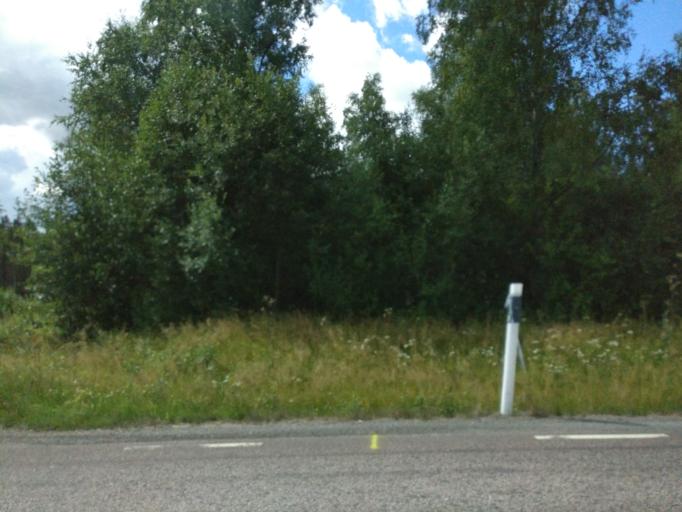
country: SE
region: Vaermland
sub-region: Hagfors Kommun
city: Ekshaerad
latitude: 60.1290
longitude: 13.5284
